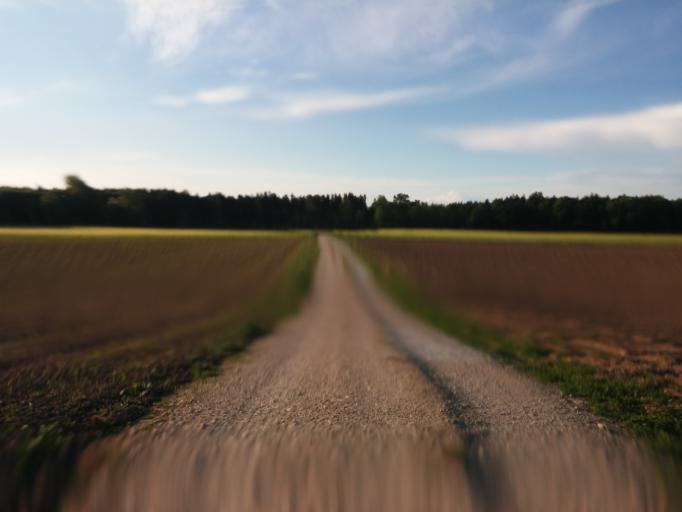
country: DE
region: Bavaria
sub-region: Upper Bavaria
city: Zorneding
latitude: 48.1066
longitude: 11.8180
